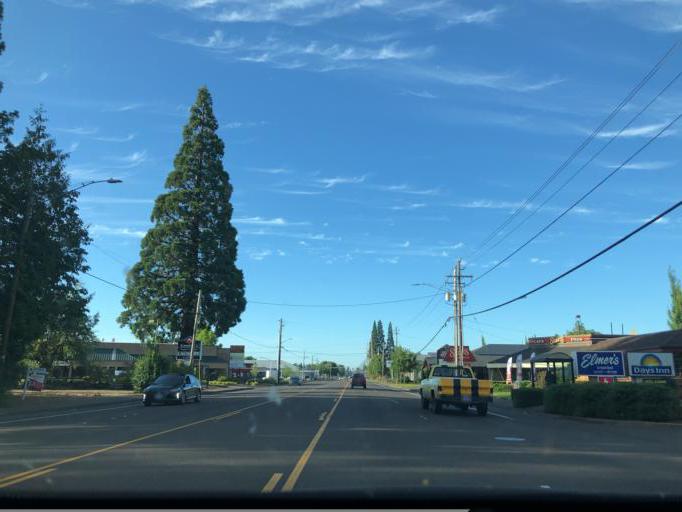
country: US
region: Oregon
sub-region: Benton County
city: Corvallis
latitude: 44.5764
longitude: -123.2617
